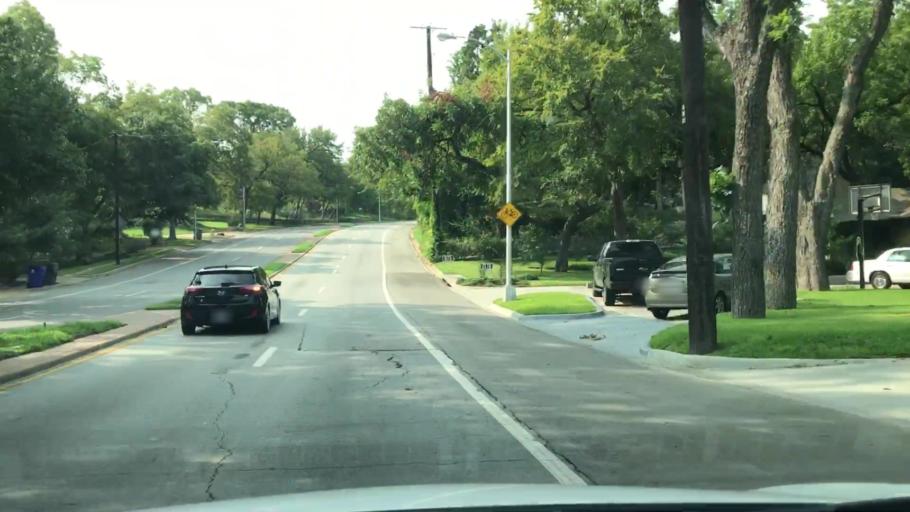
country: US
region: Texas
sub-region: Dallas County
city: Dallas
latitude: 32.7660
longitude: -96.8357
